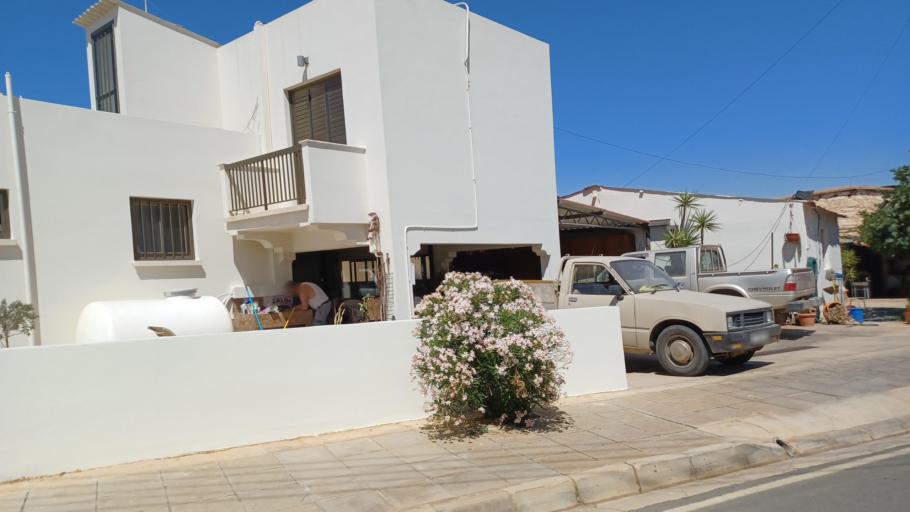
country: CY
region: Ammochostos
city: Avgorou
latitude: 35.0396
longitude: 33.8384
